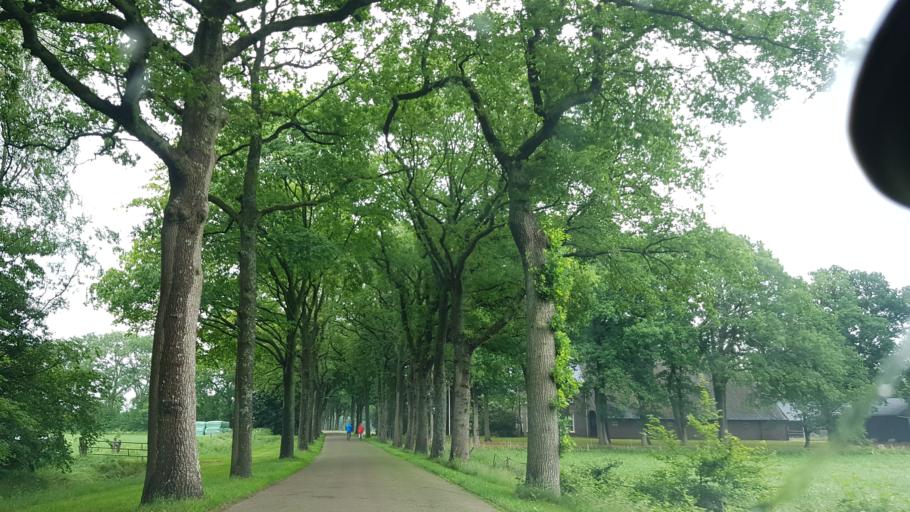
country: NL
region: Drenthe
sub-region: Gemeente Tynaarlo
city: Tynaarlo
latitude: 53.0480
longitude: 6.6208
